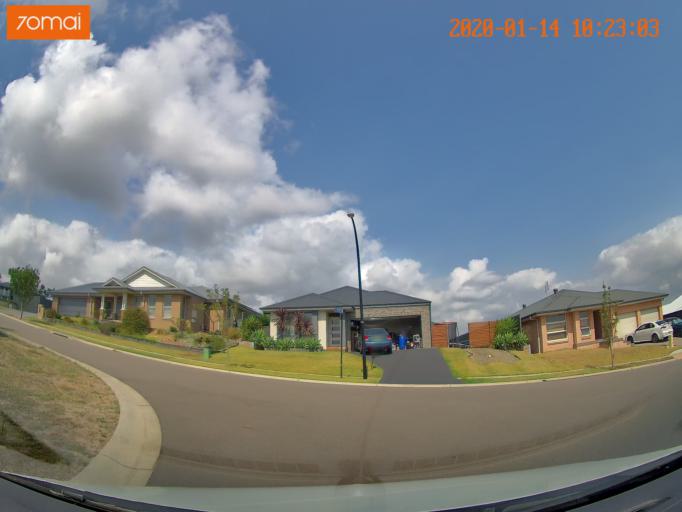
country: AU
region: New South Wales
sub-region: Lake Macquarie Shire
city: Dora Creek
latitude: -33.1099
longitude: 151.5096
